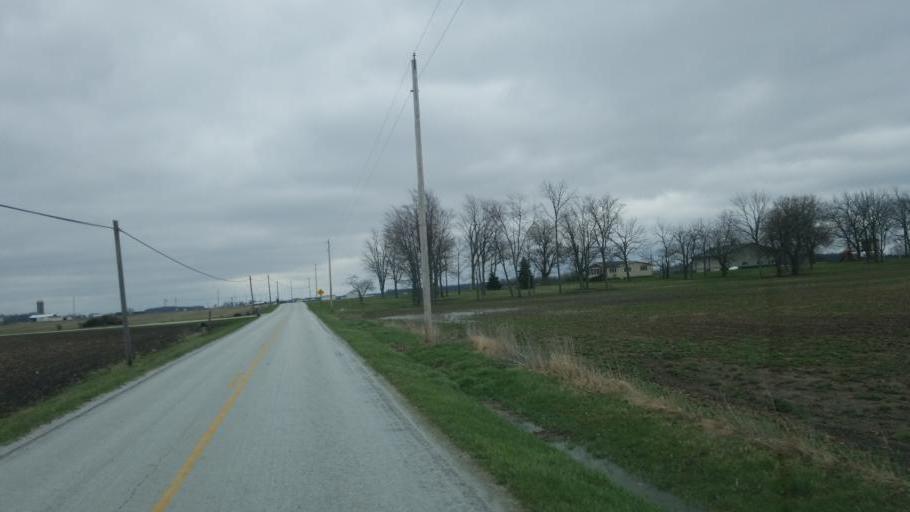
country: US
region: Ohio
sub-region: Hardin County
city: Kenton
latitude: 40.6583
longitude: -83.5416
